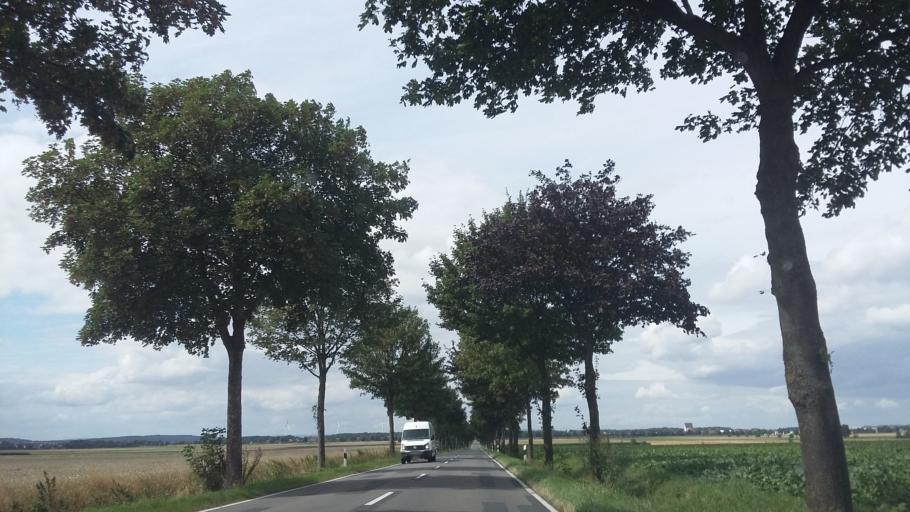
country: DE
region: Lower Saxony
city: Harsum
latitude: 52.2058
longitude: 10.0006
